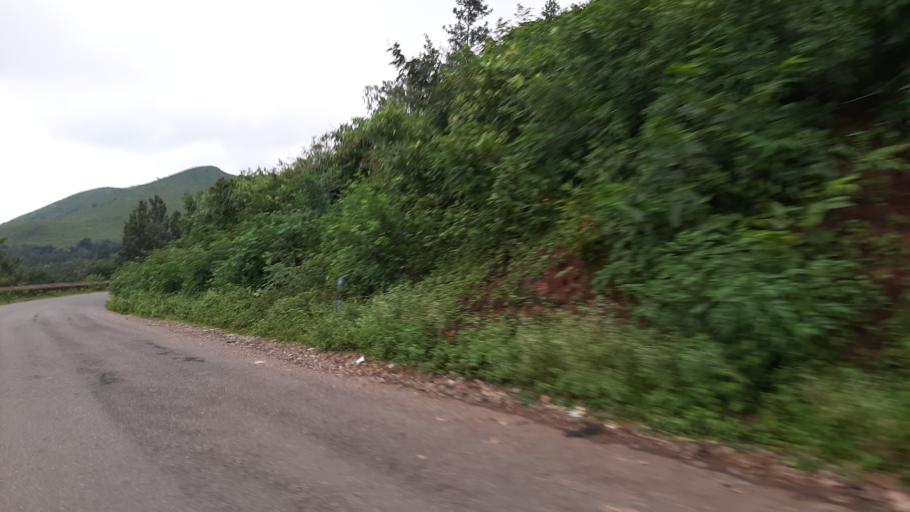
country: IN
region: Andhra Pradesh
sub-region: Vizianagaram District
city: Salur
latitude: 18.2825
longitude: 82.9414
